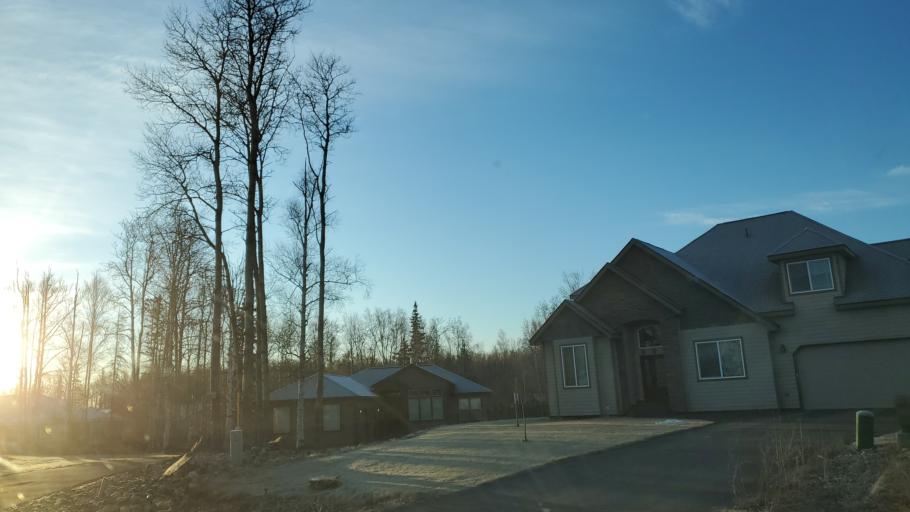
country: US
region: Alaska
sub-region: Matanuska-Susitna Borough
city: Wasilla
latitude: 61.5916
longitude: -149.4571
